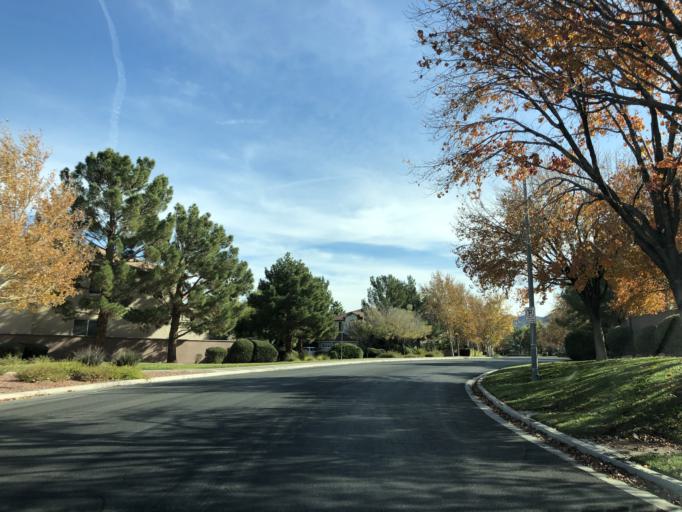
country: US
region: Nevada
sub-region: Clark County
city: Whitney
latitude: 36.0166
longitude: -115.0813
